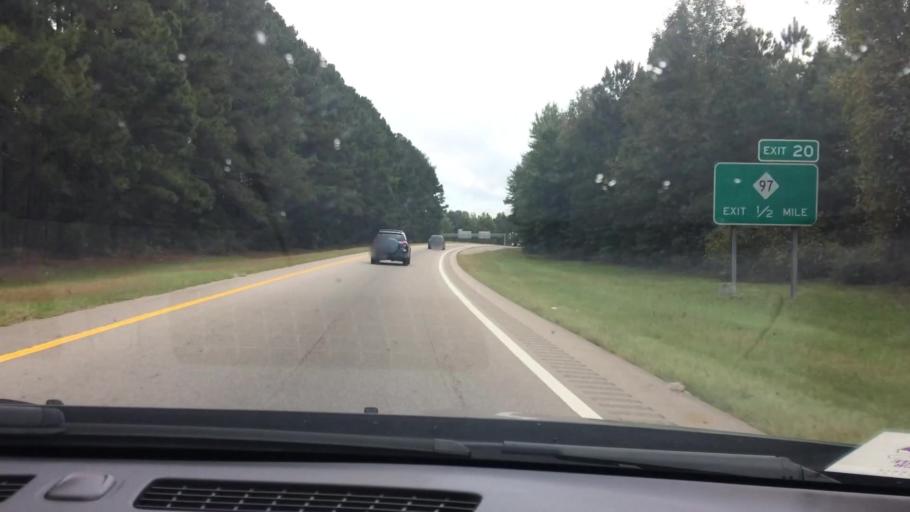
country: US
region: North Carolina
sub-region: Wake County
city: Zebulon
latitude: 35.8344
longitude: -78.3042
